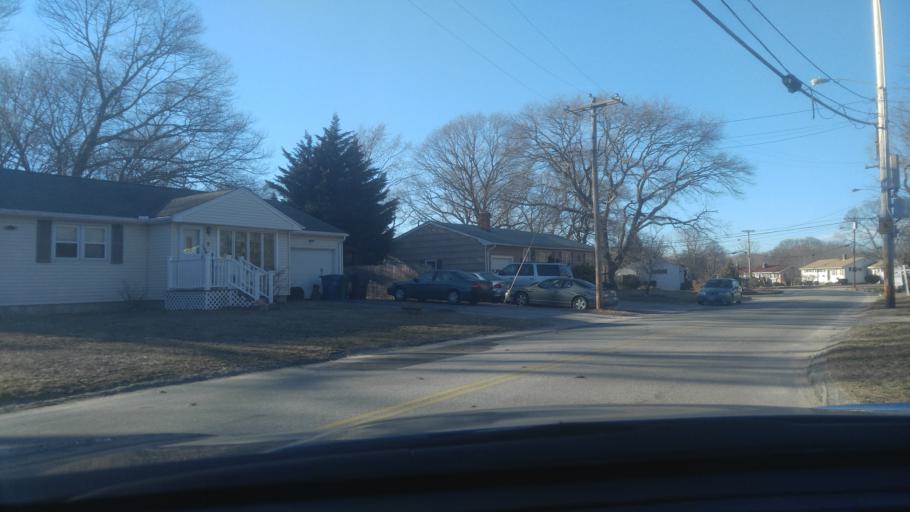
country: US
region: Rhode Island
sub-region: Kent County
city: Warwick
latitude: 41.6966
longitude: -71.4214
